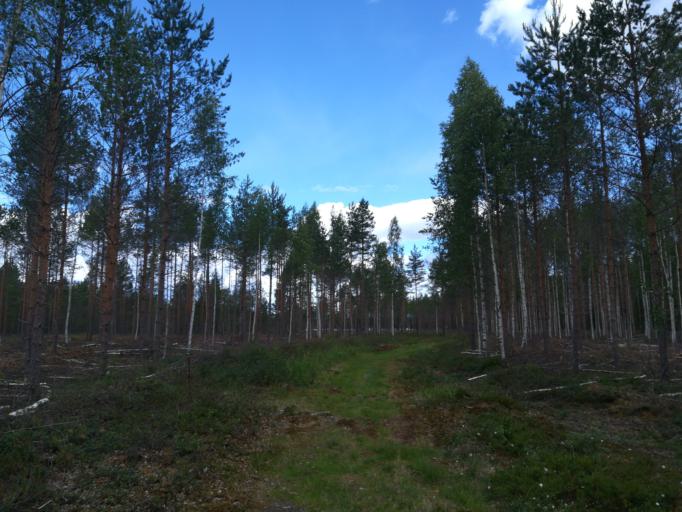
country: FI
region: Southern Savonia
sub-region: Mikkeli
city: Hirvensalmi
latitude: 61.6542
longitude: 26.7812
